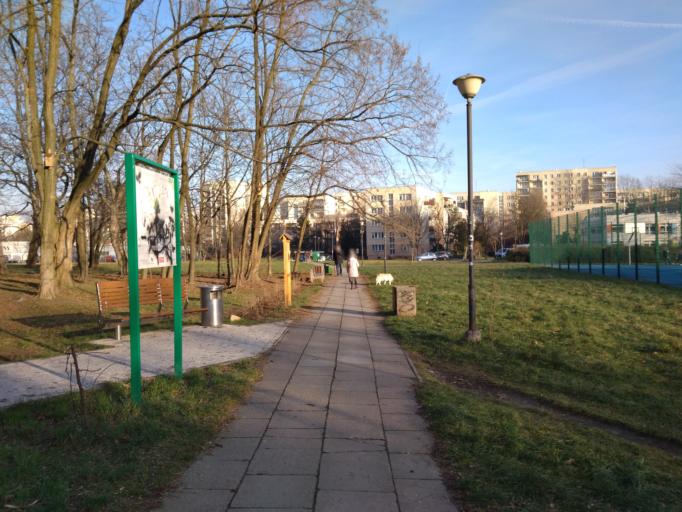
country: PL
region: Masovian Voivodeship
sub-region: Warszawa
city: Ursynow
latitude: 52.1598
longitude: 21.0246
